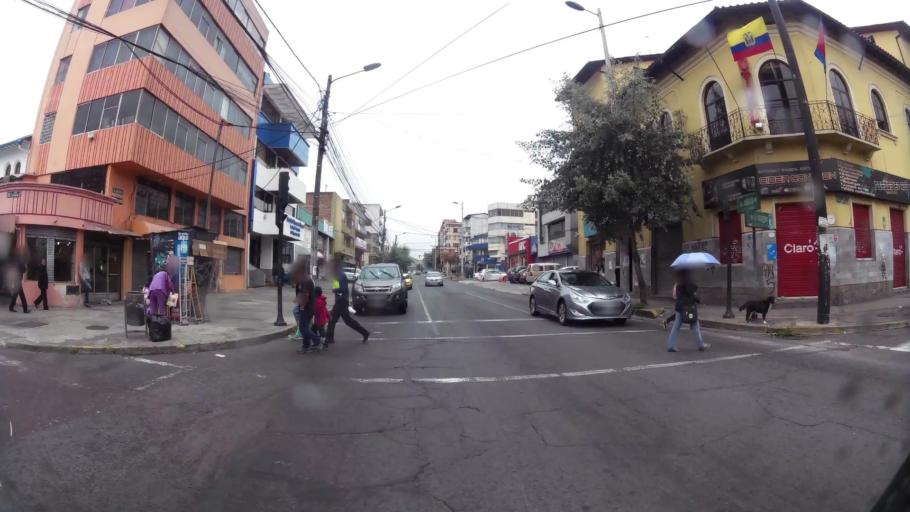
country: EC
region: Pichincha
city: Quito
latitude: -0.2048
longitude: -78.5023
